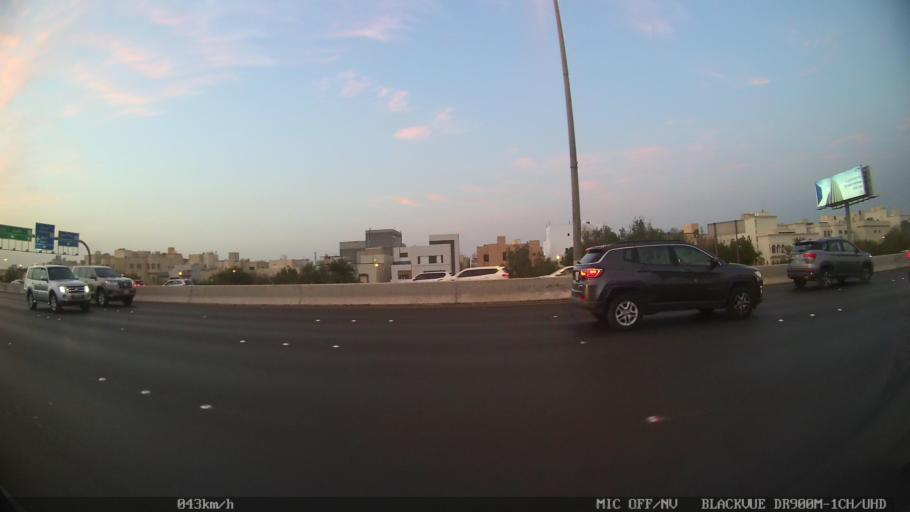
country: KW
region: Al Farwaniyah
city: Al Farwaniyah
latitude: 29.3031
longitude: 47.9688
